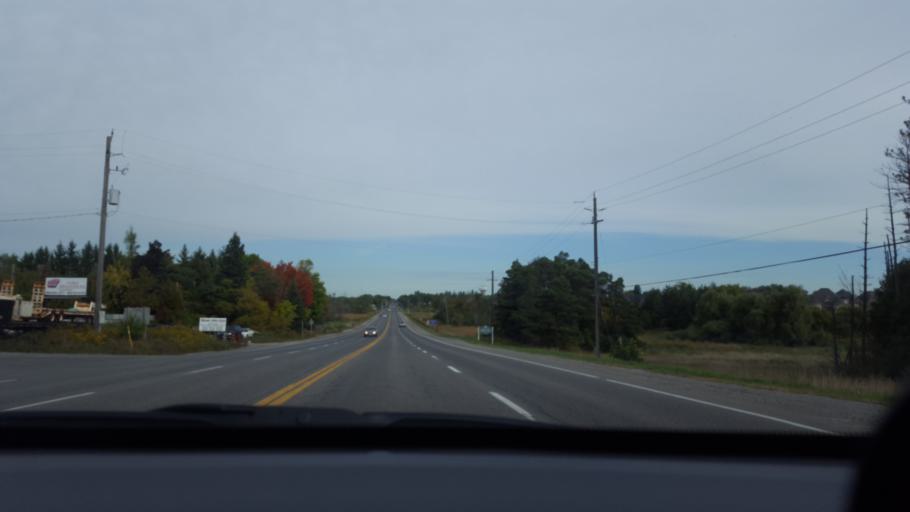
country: CA
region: Ontario
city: Vaughan
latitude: 43.9127
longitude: -79.5238
